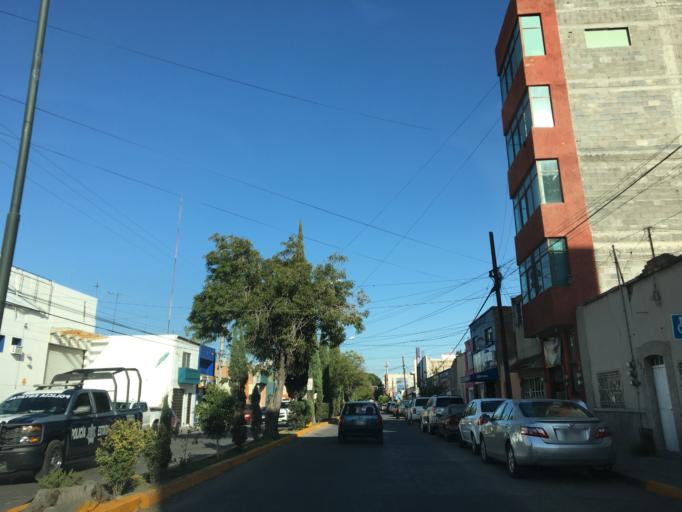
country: MX
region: San Luis Potosi
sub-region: San Luis Potosi
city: San Luis Potosi
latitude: 22.1463
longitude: -100.9864
